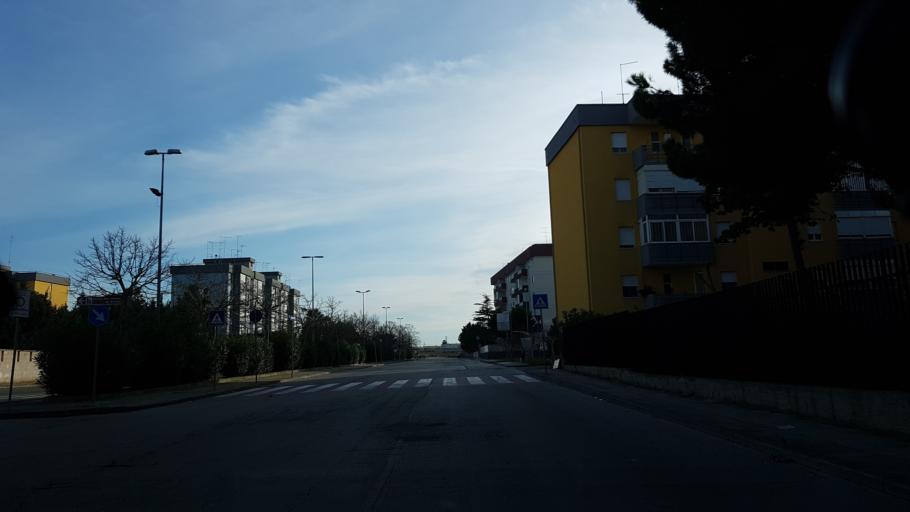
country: IT
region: Apulia
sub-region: Provincia di Brindisi
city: Brindisi
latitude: 40.6181
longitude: 17.9254
